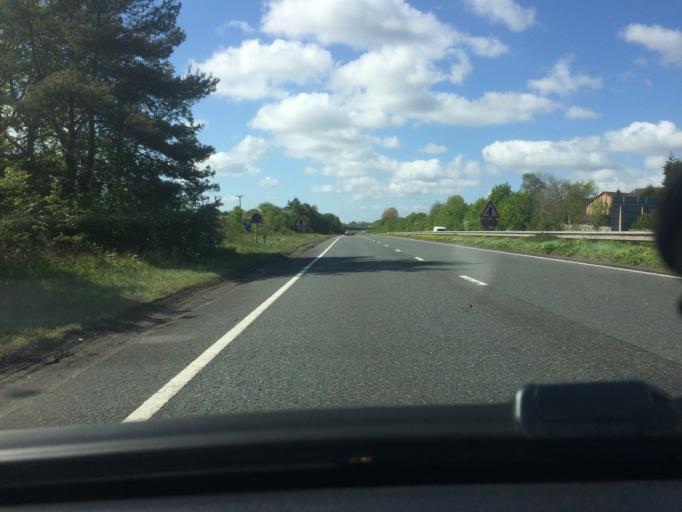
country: GB
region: England
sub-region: Cheshire West and Chester
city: Hoole
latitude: 53.1774
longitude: -2.8575
